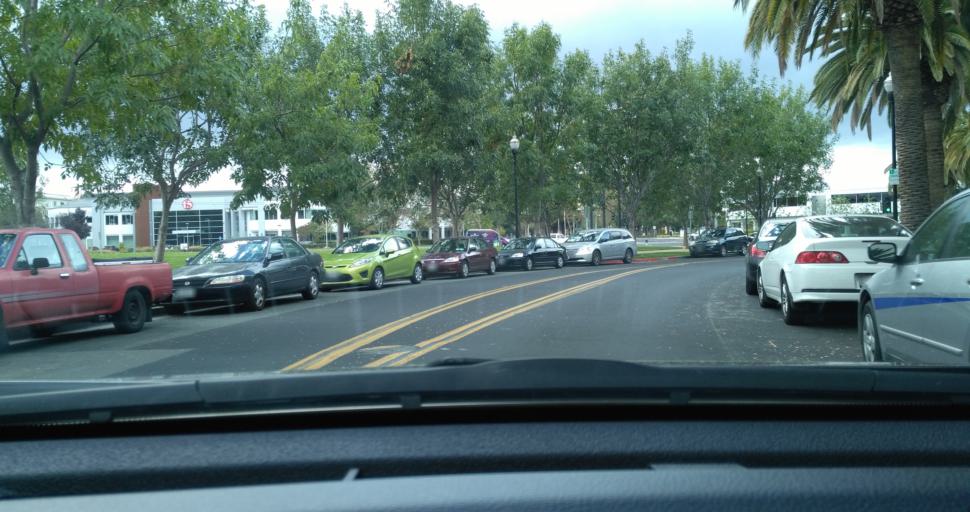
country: US
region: California
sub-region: Santa Clara County
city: Milpitas
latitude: 37.4064
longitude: -121.9412
